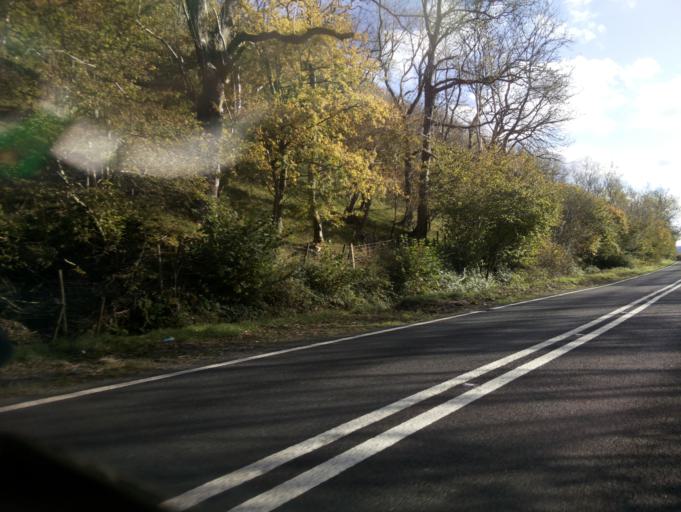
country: GB
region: Wales
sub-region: Merthyr Tydfil County Borough
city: Merthyr Tydfil
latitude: 51.7859
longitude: -3.4257
